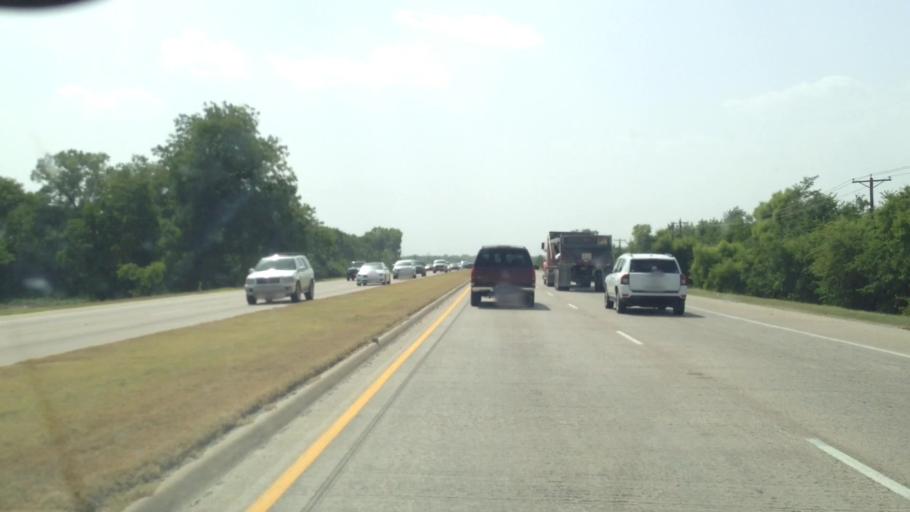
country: US
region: Texas
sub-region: Collin County
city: McKinney
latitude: 33.1995
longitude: -96.5802
